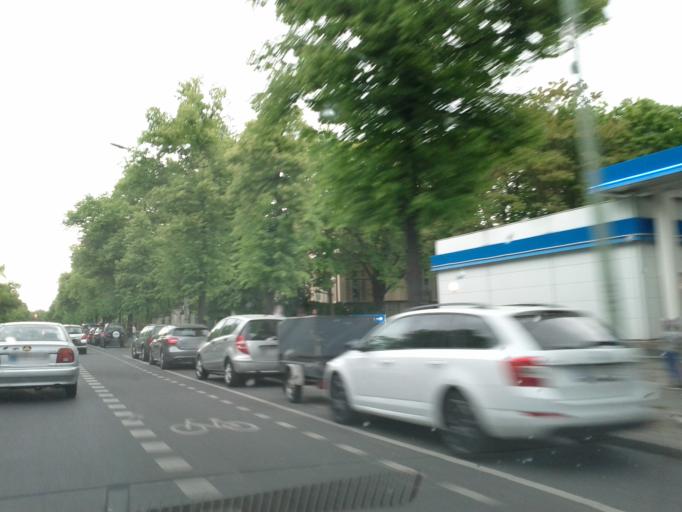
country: DE
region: Berlin
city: Westend
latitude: 52.5134
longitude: 13.2659
